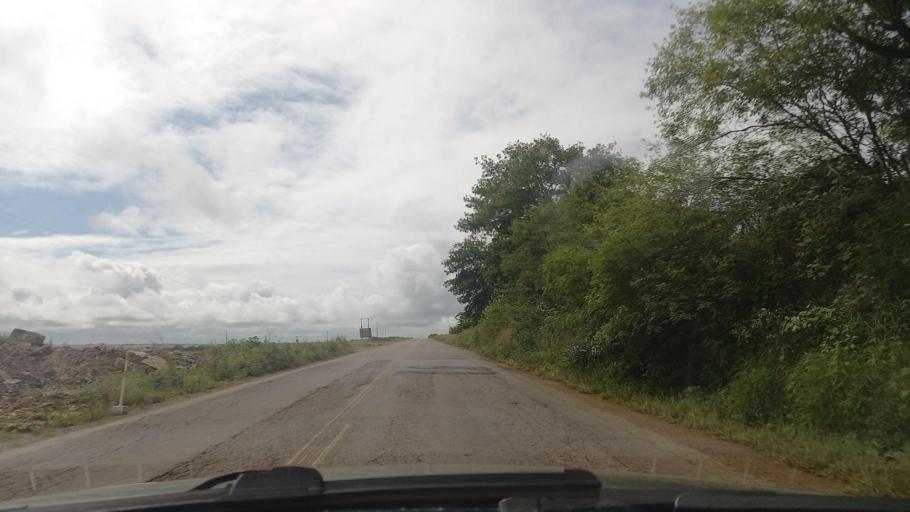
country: BR
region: Alagoas
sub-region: Batalha
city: Batalha
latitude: -9.6648
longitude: -37.1617
